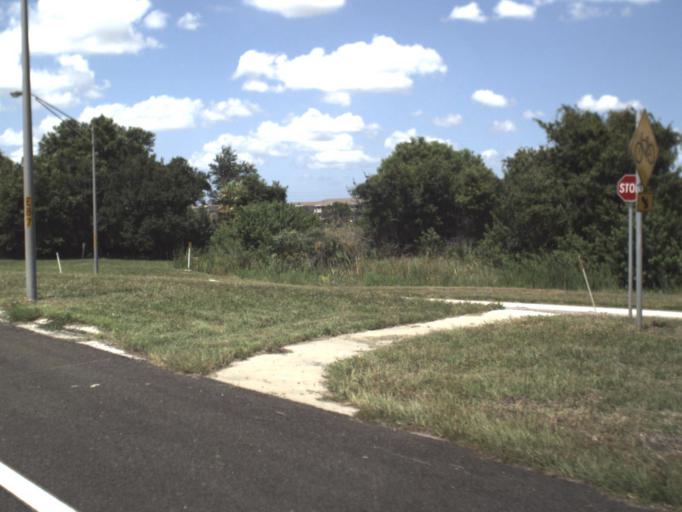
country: US
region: Florida
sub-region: Pinellas County
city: Lealman
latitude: 27.8506
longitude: -82.6685
